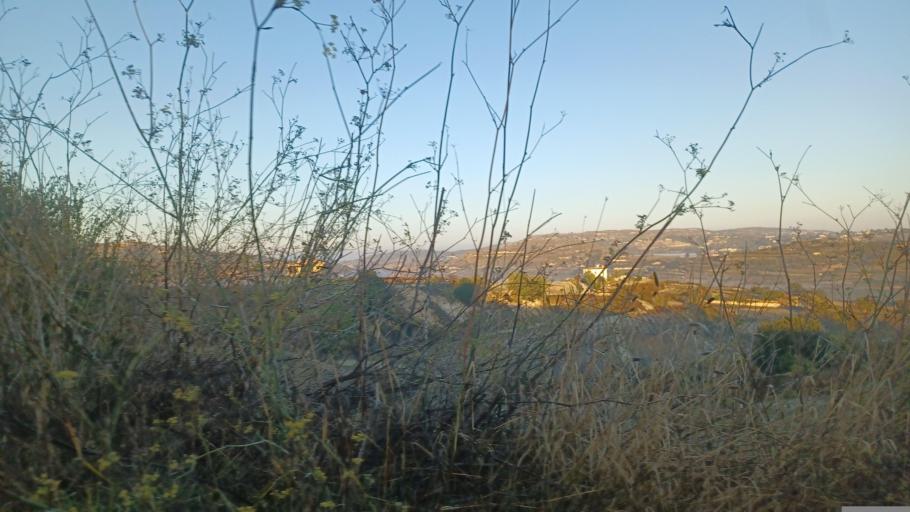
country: CY
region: Pafos
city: Mesogi
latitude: 34.8665
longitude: 32.5068
